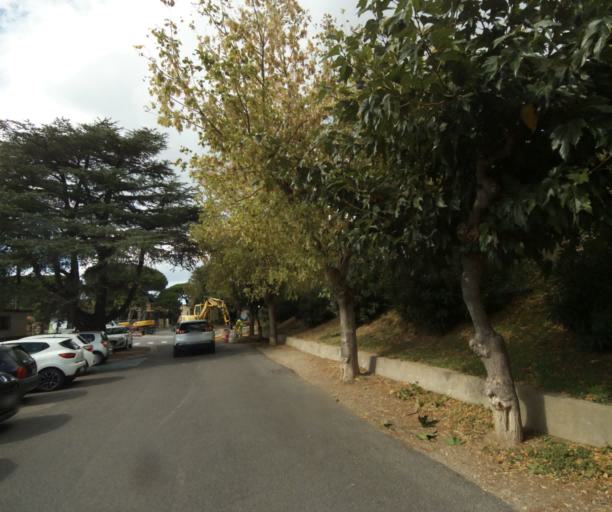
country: FR
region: Languedoc-Roussillon
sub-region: Departement des Pyrenees-Orientales
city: Argelers
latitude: 42.5441
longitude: 3.0211
